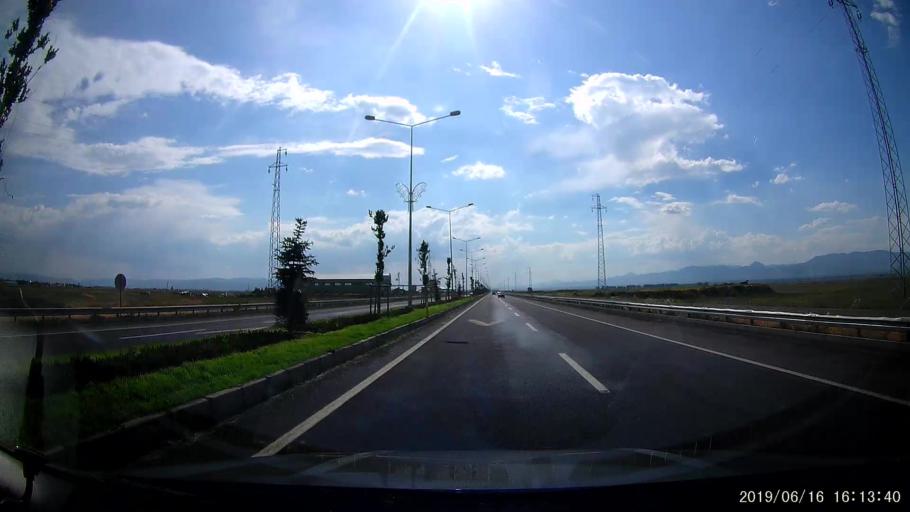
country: TR
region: Erzurum
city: Erzurum
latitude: 39.9598
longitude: 41.2665
